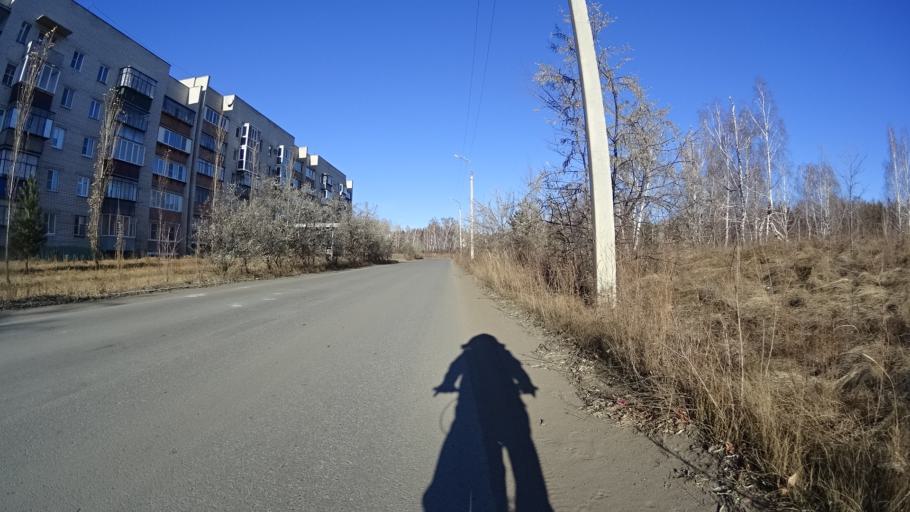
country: RU
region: Chelyabinsk
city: Troitsk
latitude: 54.0522
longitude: 61.6406
